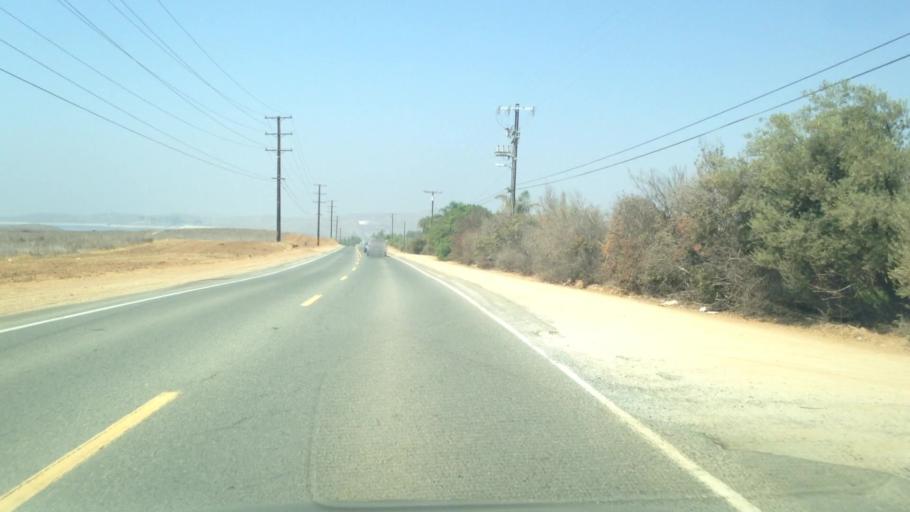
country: US
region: California
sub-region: Riverside County
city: Woodcrest
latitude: 33.8583
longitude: -117.4096
